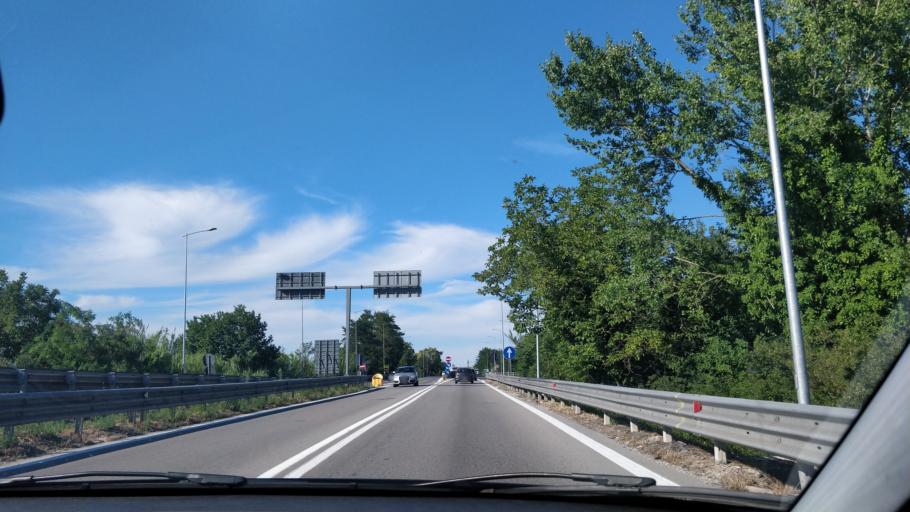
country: IT
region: Abruzzo
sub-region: Provincia di Chieti
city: Casalincontrada
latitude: 42.3382
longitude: 14.1291
